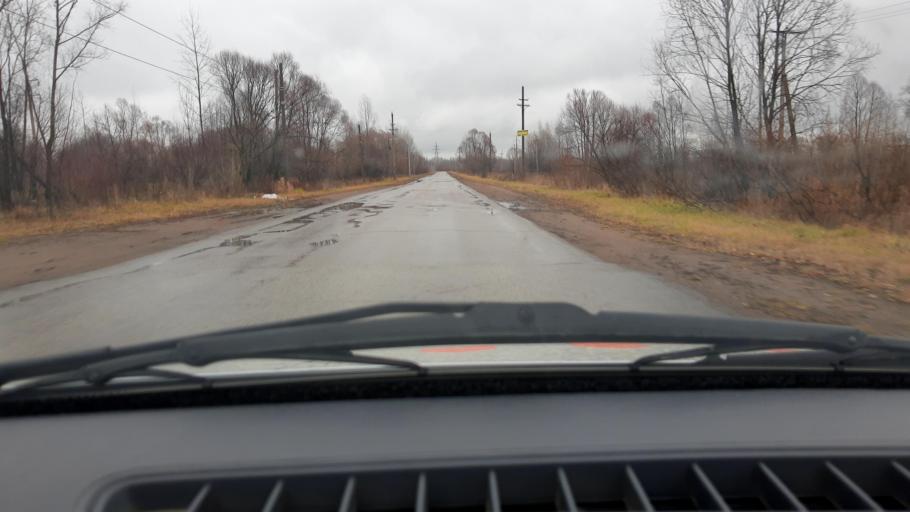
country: RU
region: Bashkortostan
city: Ufa
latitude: 54.8100
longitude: 56.1669
